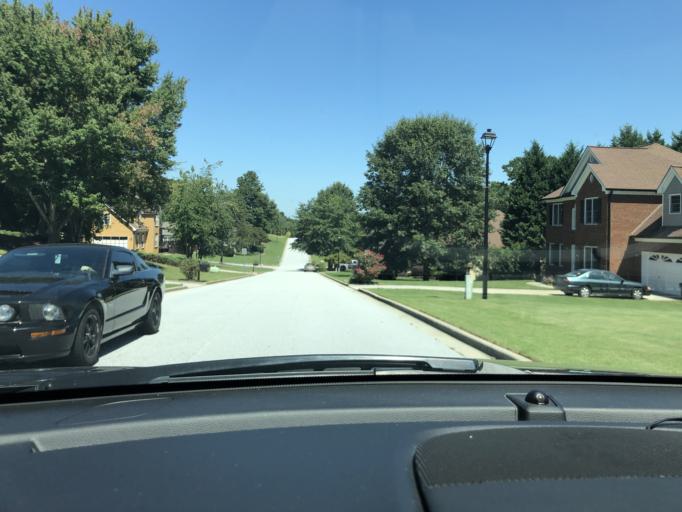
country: US
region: Georgia
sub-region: Gwinnett County
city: Grayson
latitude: 33.9074
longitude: -83.9211
